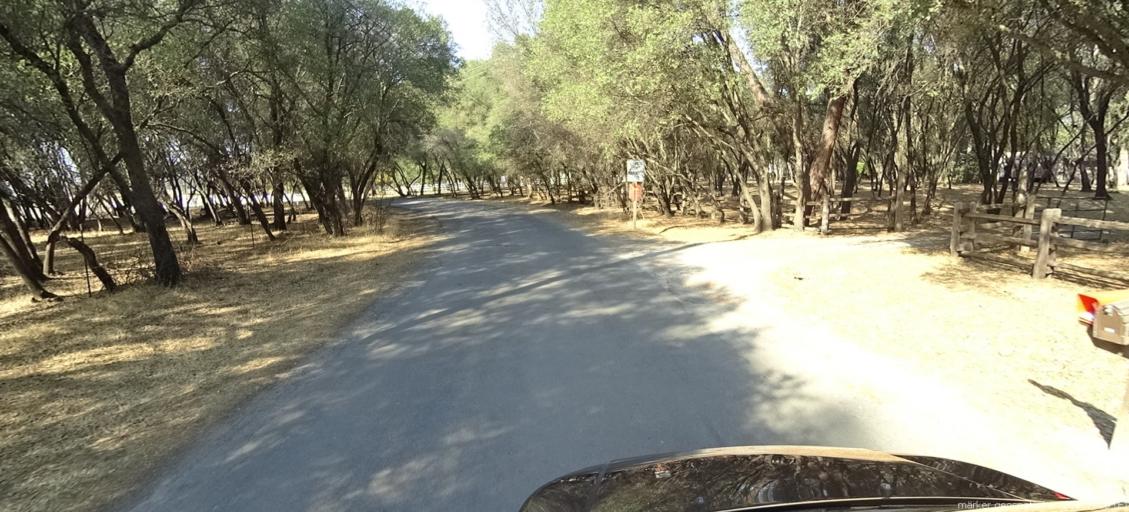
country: US
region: California
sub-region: Shasta County
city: Palo Cedro
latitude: 40.5782
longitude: -122.2277
